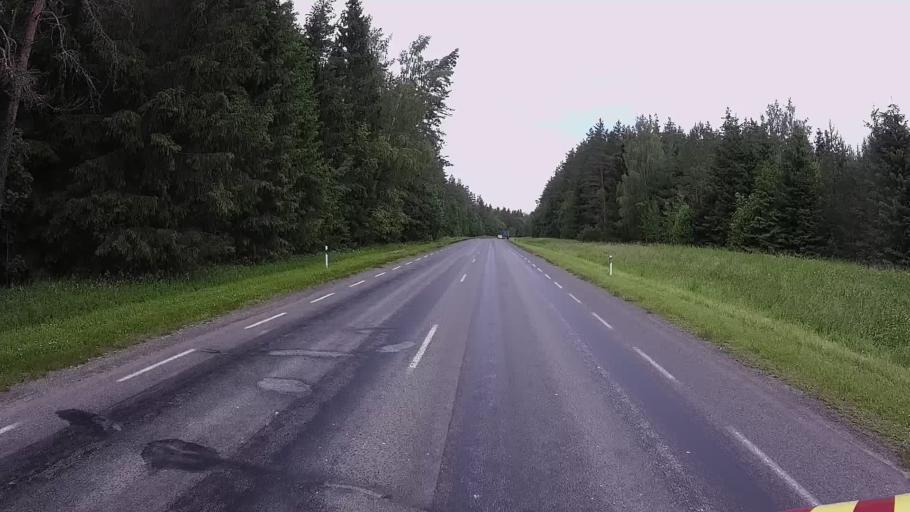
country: EE
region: Viljandimaa
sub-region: Viljandi linn
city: Viljandi
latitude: 58.2956
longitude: 25.5772
